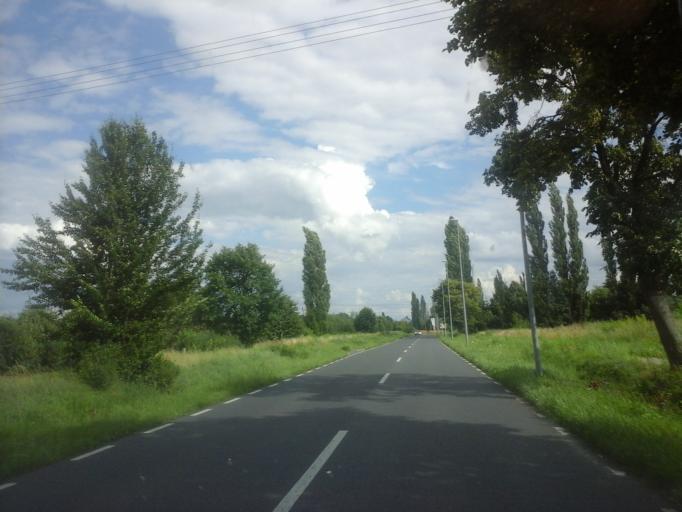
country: PL
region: West Pomeranian Voivodeship
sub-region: Powiat stargardzki
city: Stargard Szczecinski
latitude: 53.3554
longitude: 15.0146
